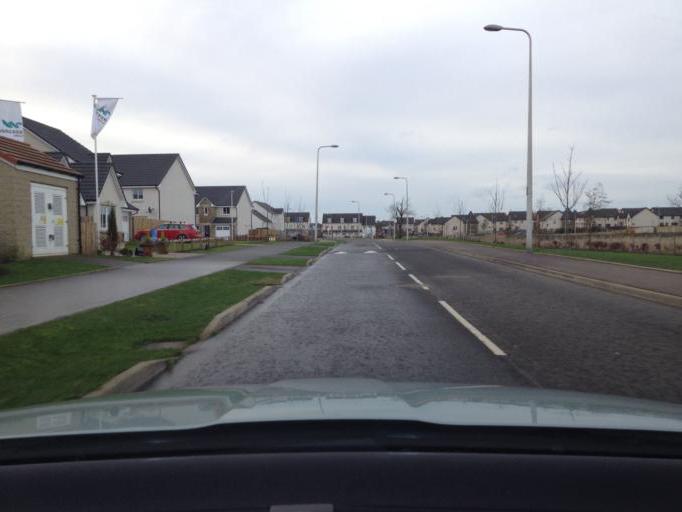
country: GB
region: Scotland
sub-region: Edinburgh
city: Kirkliston
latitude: 55.9606
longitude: -3.3999
